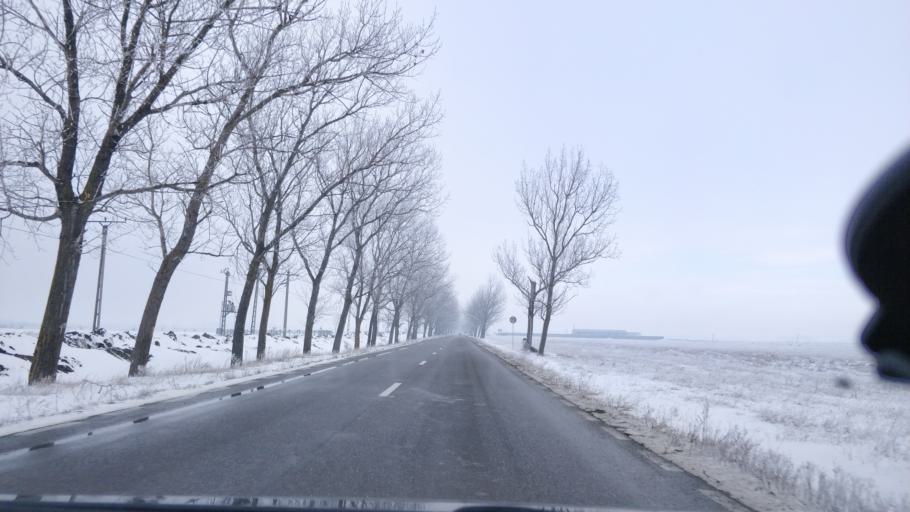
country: RO
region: Vrancea
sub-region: Comuna Vanatori
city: Jorasti
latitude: 45.6974
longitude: 27.2537
